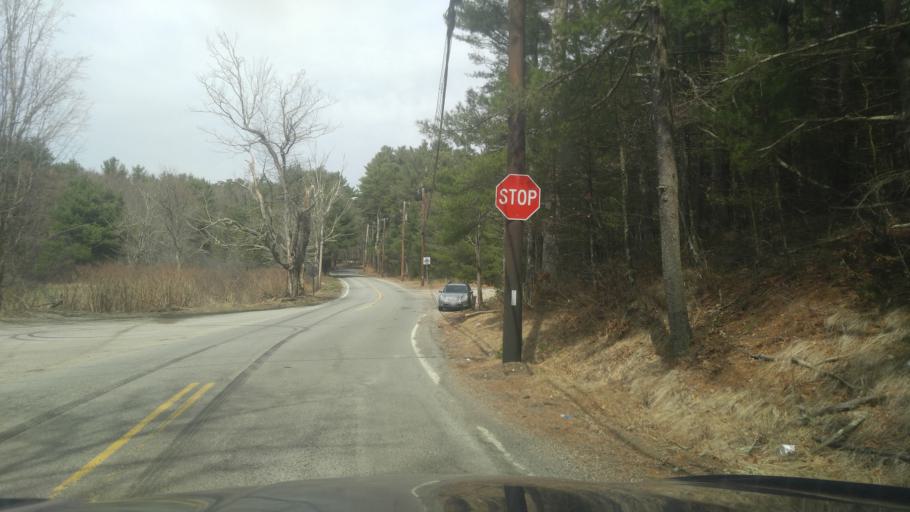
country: US
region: Rhode Island
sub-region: Washington County
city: Exeter
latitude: 41.6398
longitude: -71.5731
